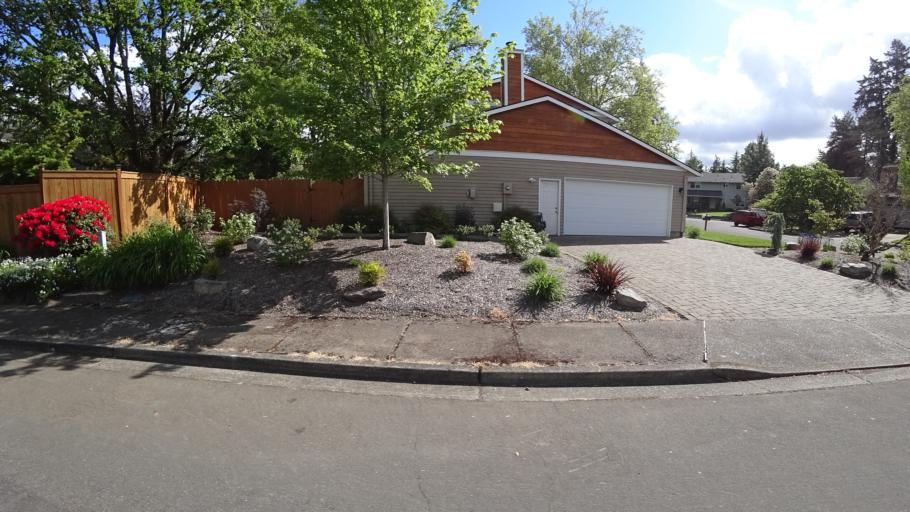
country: US
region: Oregon
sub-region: Washington County
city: Beaverton
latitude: 45.4633
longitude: -122.8376
